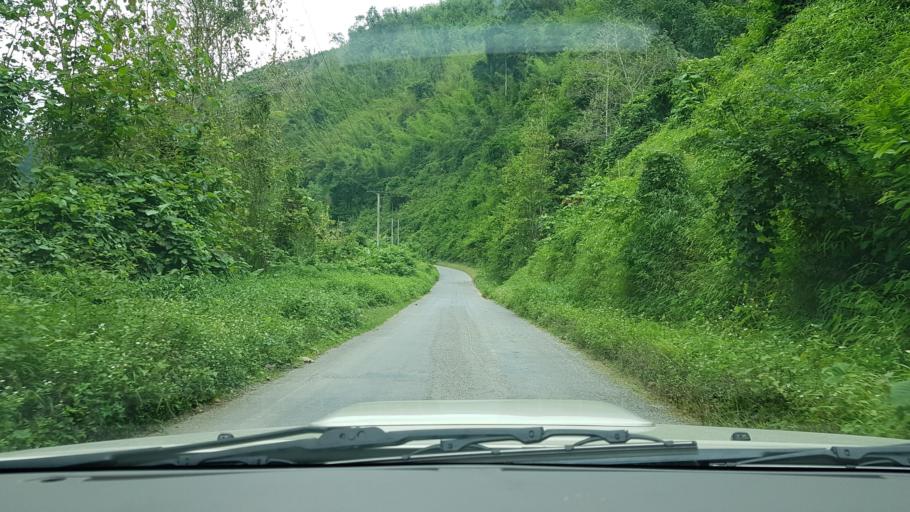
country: LA
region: Phongsali
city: Khoa
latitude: 21.0763
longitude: 102.3776
